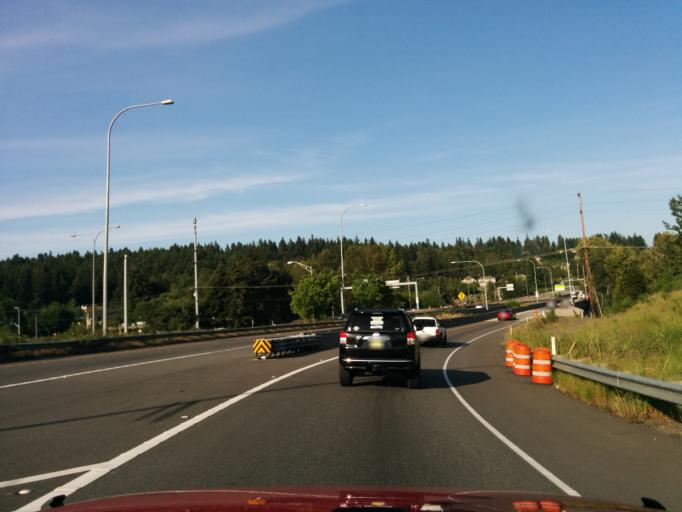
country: US
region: Washington
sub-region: King County
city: Bellevue
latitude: 47.6315
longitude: -122.1870
